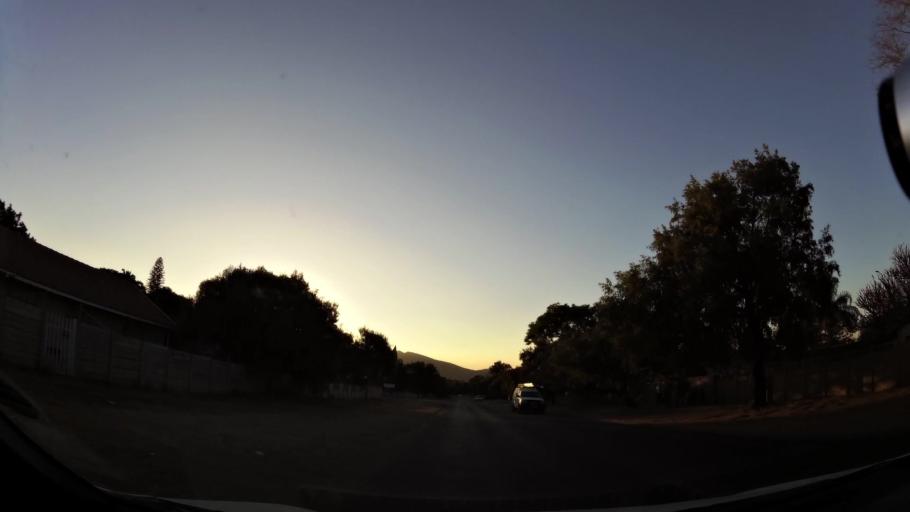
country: ZA
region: North-West
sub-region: Bojanala Platinum District Municipality
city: Rustenburg
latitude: -25.6801
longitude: 27.2202
